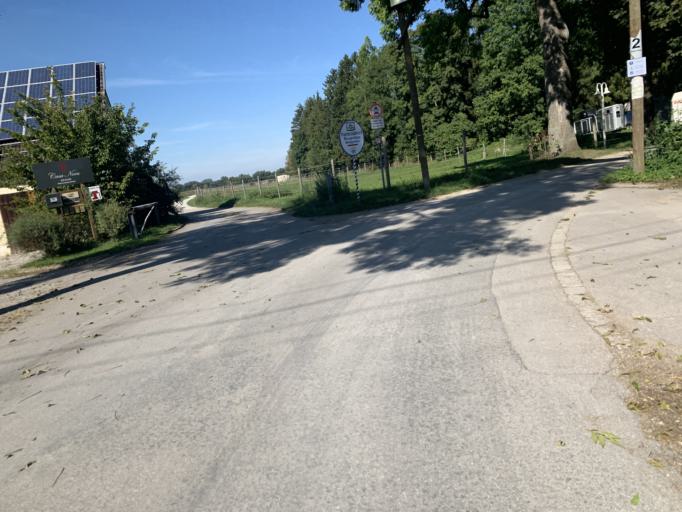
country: DE
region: Bavaria
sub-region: Swabia
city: Kissing
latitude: 48.3149
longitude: 10.9819
